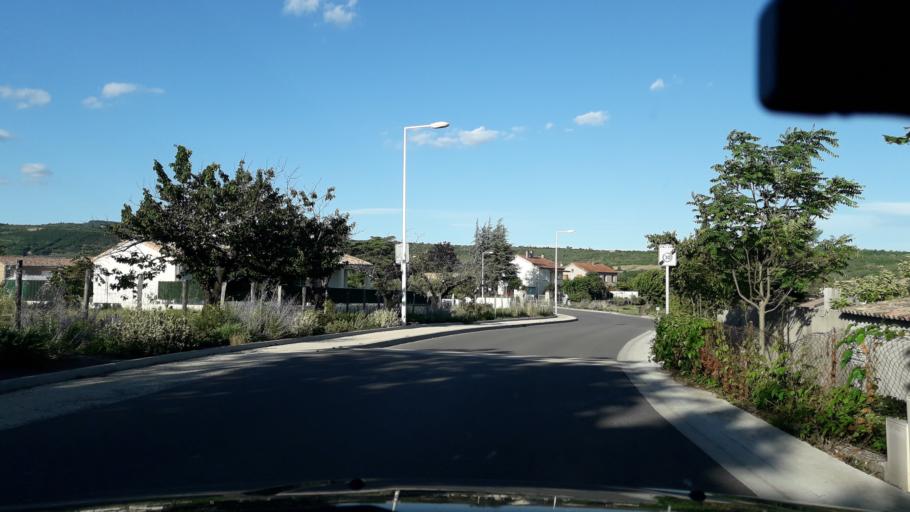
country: FR
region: Rhone-Alpes
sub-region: Departement de l'Ardeche
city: Lavilledieu
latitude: 44.5791
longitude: 4.4549
